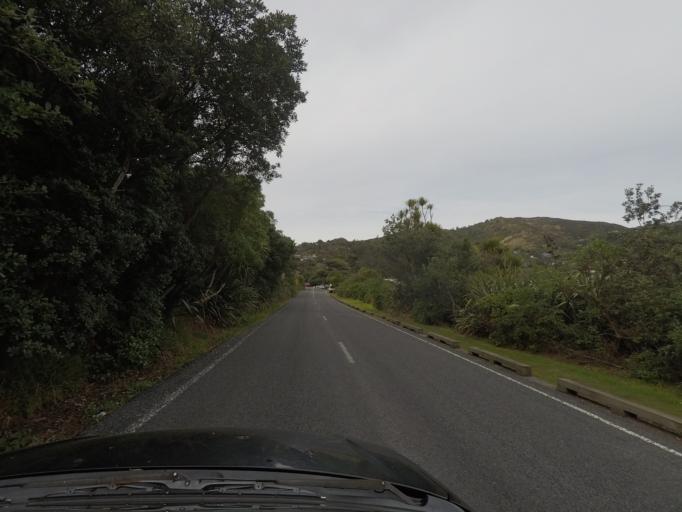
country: NZ
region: Auckland
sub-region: Auckland
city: Muriwai Beach
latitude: -36.9530
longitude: 174.4710
